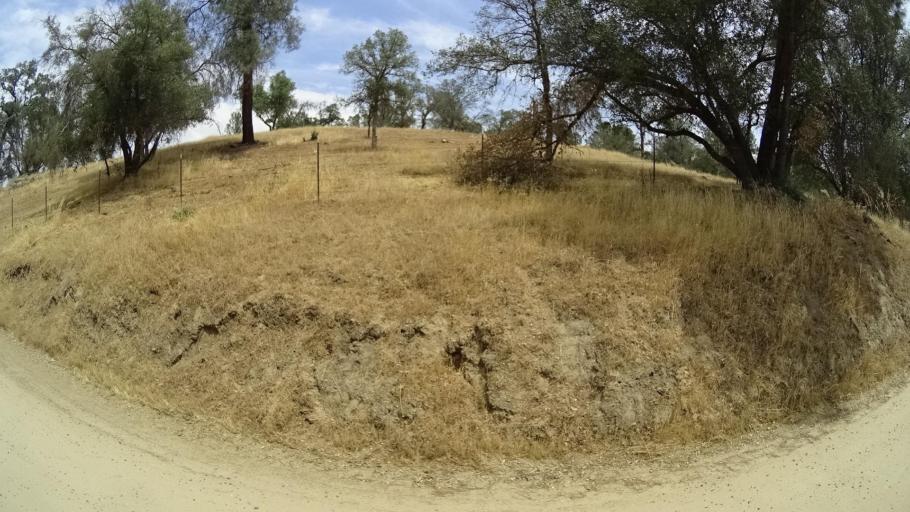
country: US
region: California
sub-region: Madera County
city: Ahwahnee
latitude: 37.3295
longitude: -119.8854
